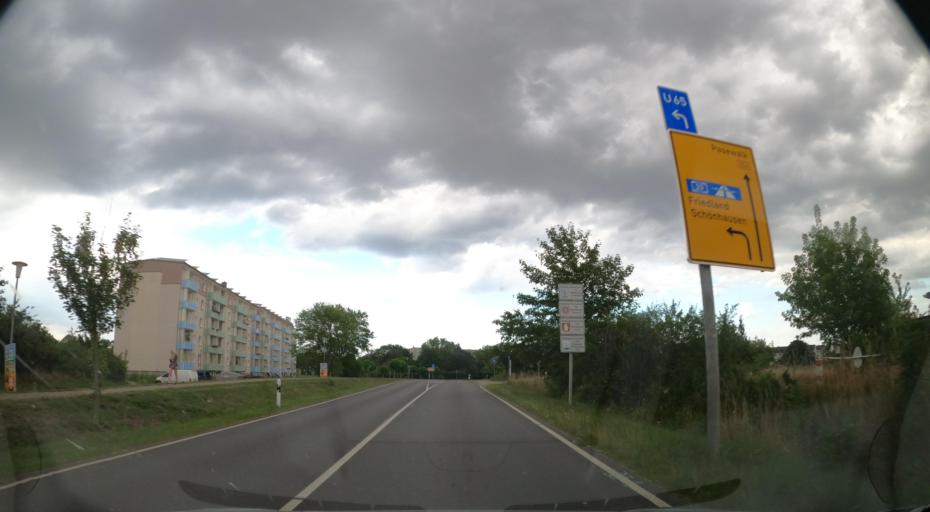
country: DE
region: Mecklenburg-Vorpommern
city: Strasburg
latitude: 53.5050
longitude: 13.7380
